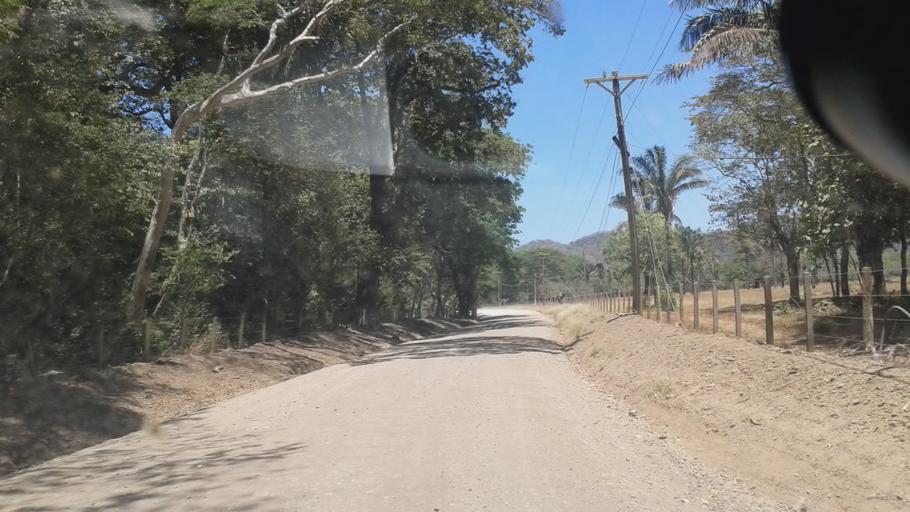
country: CR
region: Guanacaste
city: Samara
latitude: 9.9981
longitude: -85.6918
